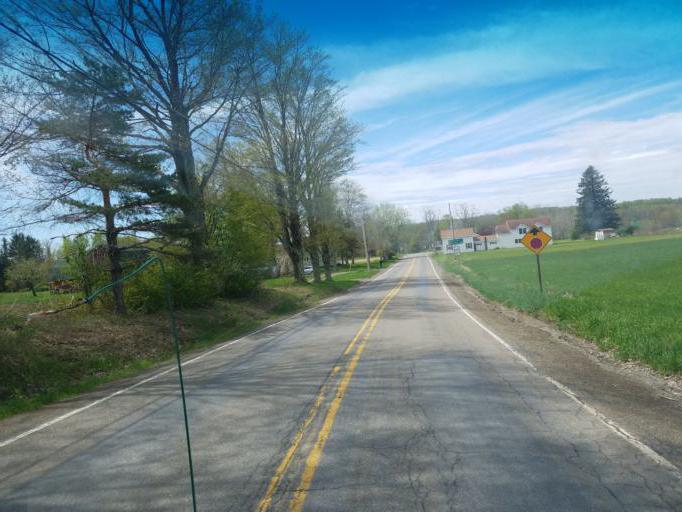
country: US
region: Pennsylvania
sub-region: Tioga County
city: Wellsboro
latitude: 41.7039
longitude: -77.3894
